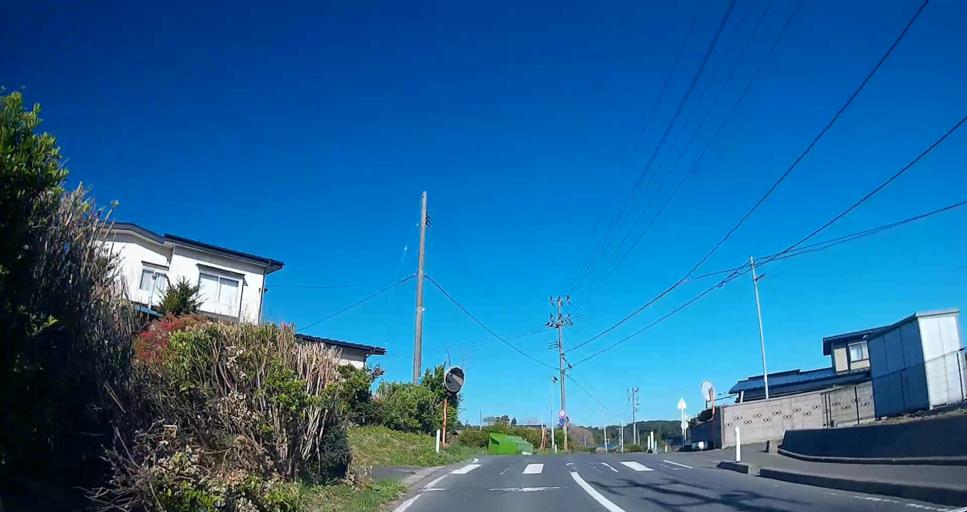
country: JP
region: Aomori
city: Hachinohe
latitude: 40.5157
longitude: 141.5899
